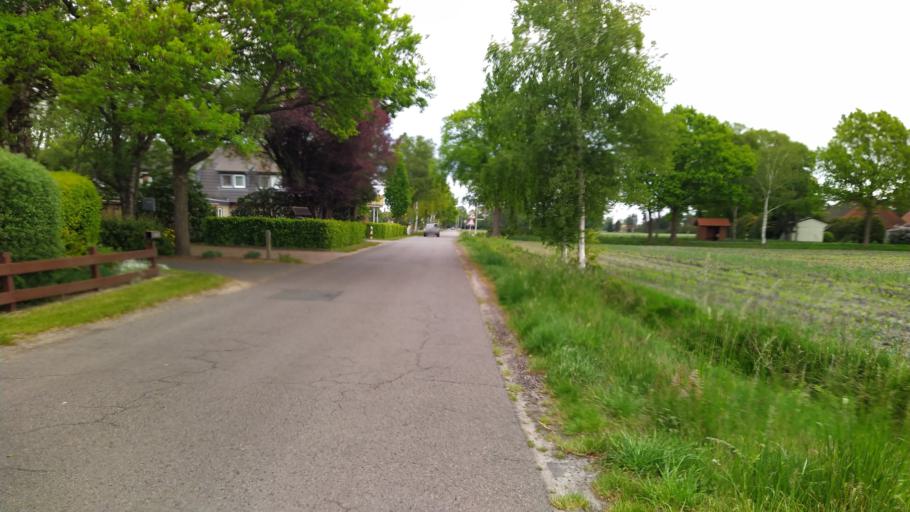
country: DE
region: Lower Saxony
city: Grasberg
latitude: 53.1865
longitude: 9.0133
